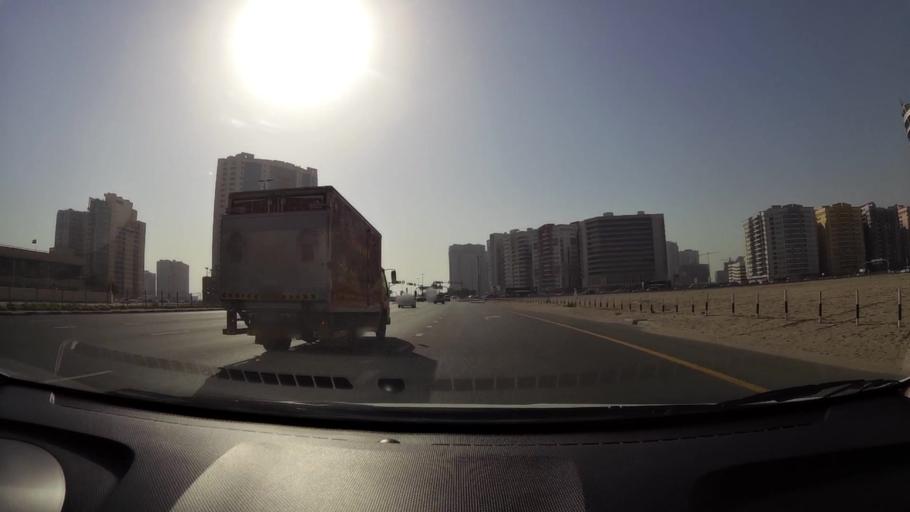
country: AE
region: Ash Shariqah
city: Sharjah
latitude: 25.2873
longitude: 55.3684
